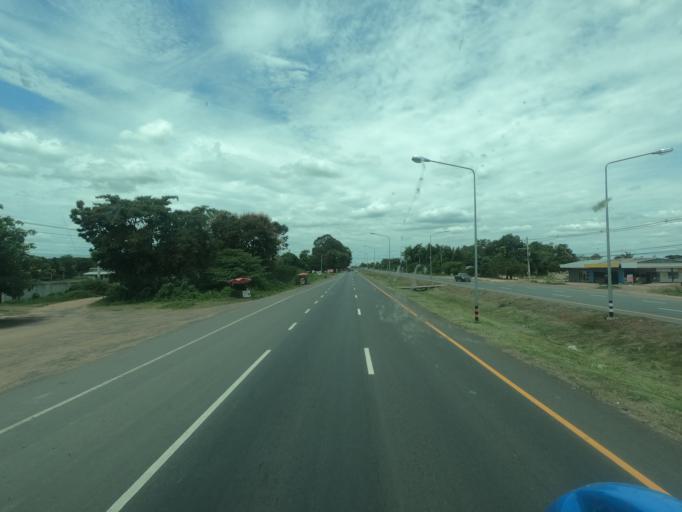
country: TH
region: Buriram
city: Prakhon Chai
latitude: 14.6202
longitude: 103.1798
